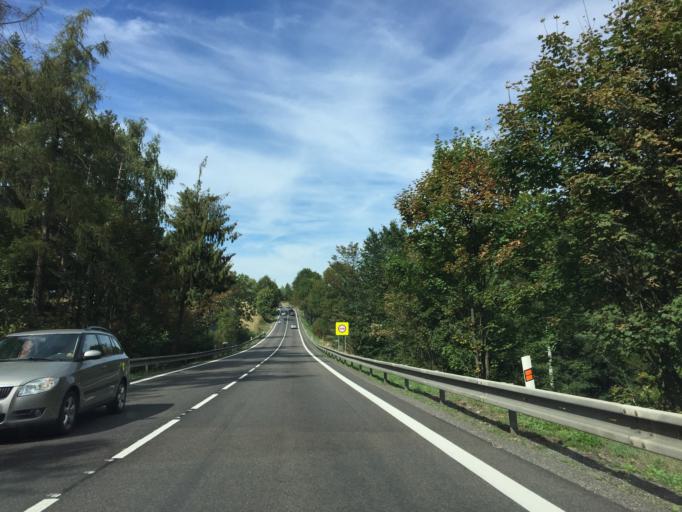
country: CZ
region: Central Bohemia
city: Votice
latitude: 49.5942
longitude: 14.6617
